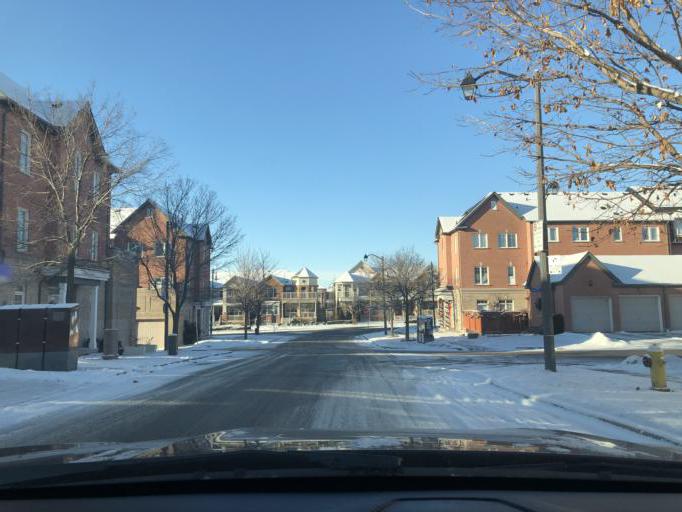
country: CA
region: Ontario
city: Pickering
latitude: 43.7789
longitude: -79.1353
